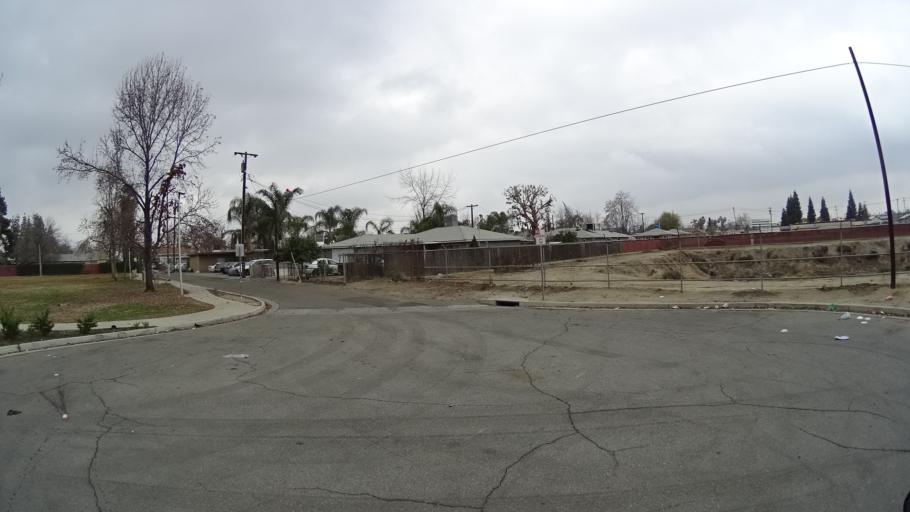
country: US
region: California
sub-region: Kern County
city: Bakersfield
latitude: 35.3844
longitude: -119.0070
